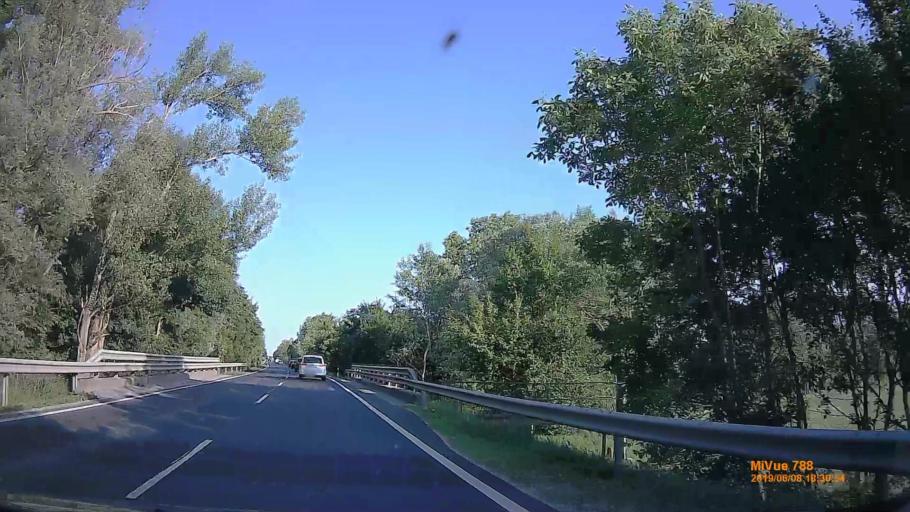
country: HU
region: Vas
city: Sarvar
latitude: 47.3679
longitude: 16.8887
